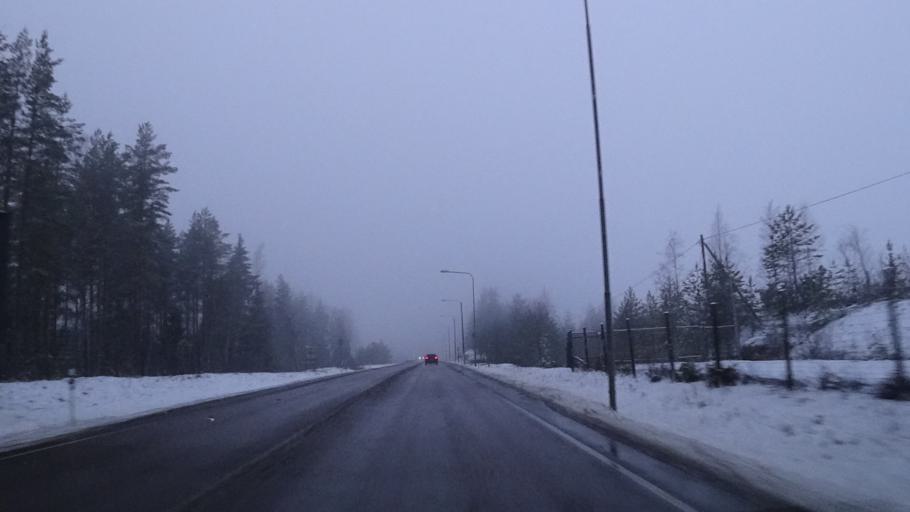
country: FI
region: Paijanne Tavastia
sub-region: Lahti
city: Hollola
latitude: 60.9862
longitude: 25.4035
